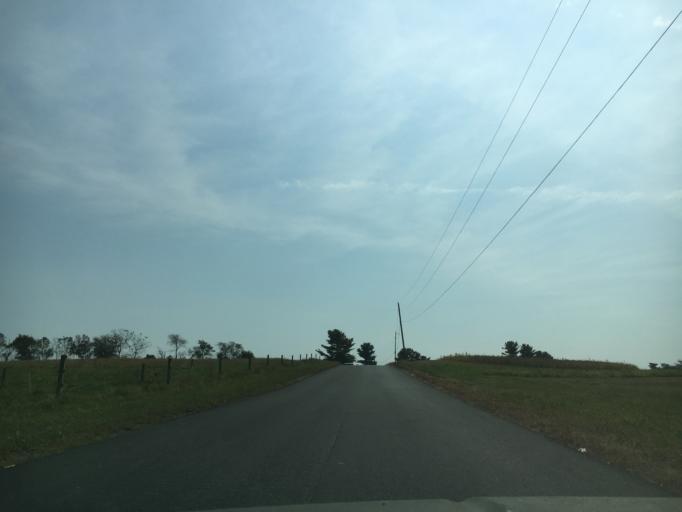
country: US
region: Pennsylvania
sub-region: Berks County
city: Topton
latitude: 40.5494
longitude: -75.7150
